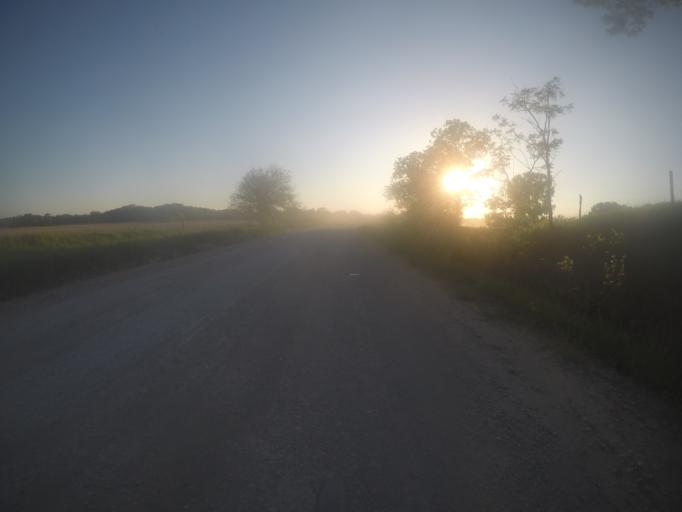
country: US
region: Kansas
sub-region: Riley County
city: Manhattan
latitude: 39.2294
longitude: -96.5470
